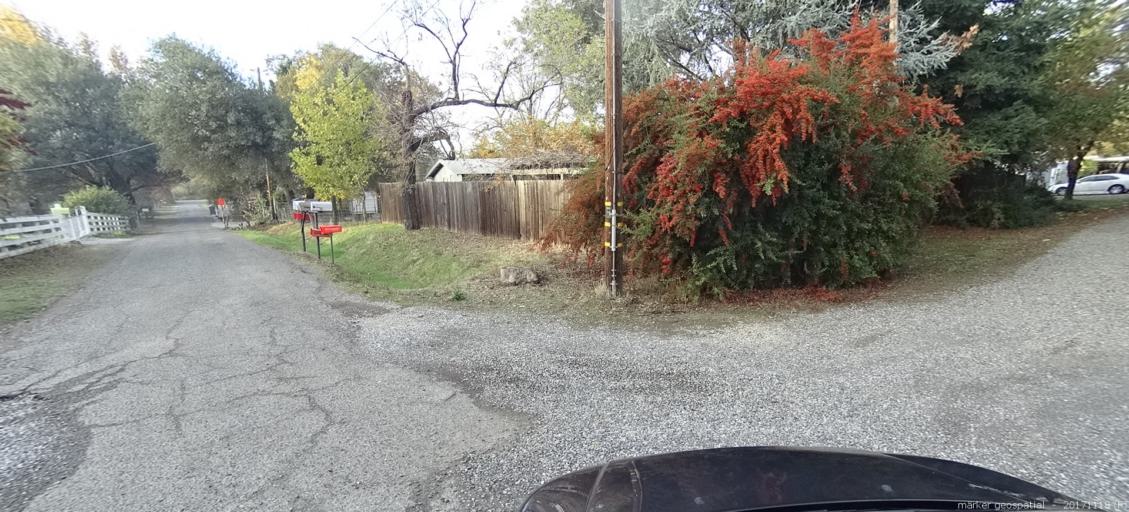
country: US
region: California
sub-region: Shasta County
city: Anderson
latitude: 40.4638
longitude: -122.3257
